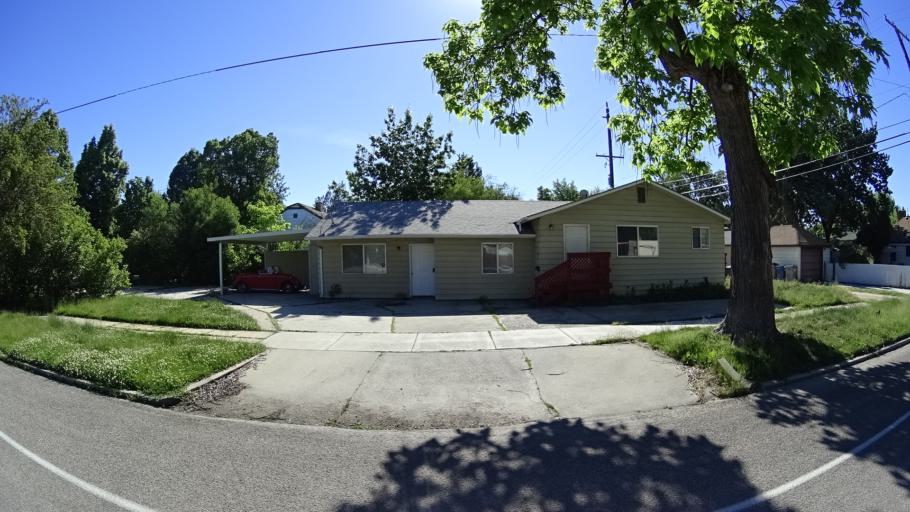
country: US
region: Idaho
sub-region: Ada County
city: Boise
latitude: 43.6242
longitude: -116.2184
